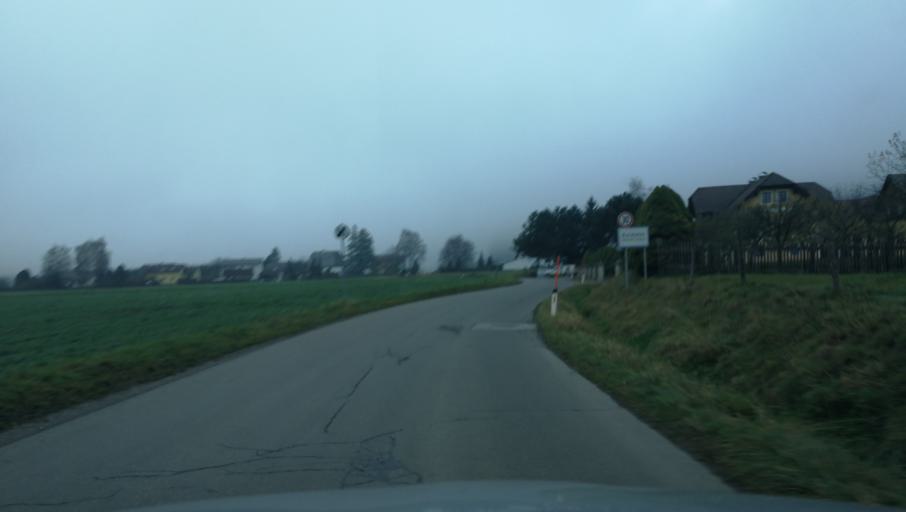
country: AT
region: Styria
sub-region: Politischer Bezirk Leoben
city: Trofaiach
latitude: 47.4289
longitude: 14.9784
